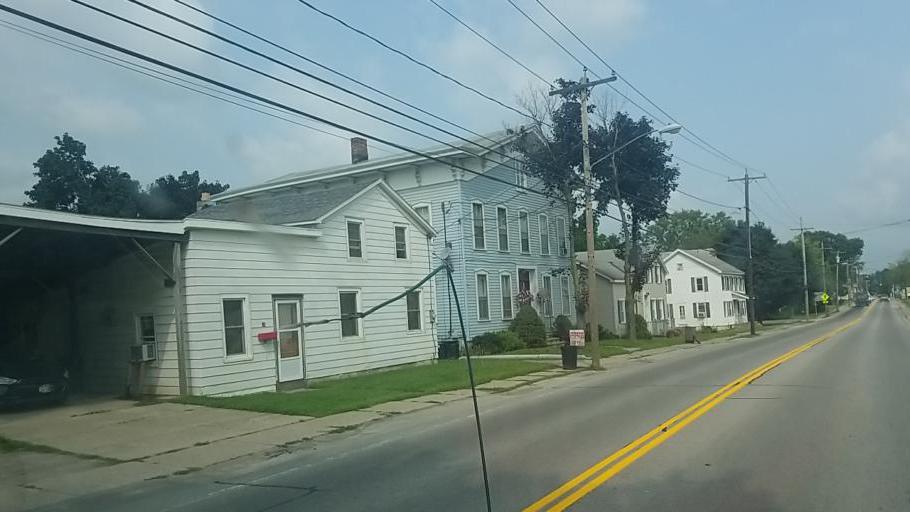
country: US
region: New York
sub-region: Montgomery County
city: Fort Plain
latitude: 42.9321
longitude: -74.6120
